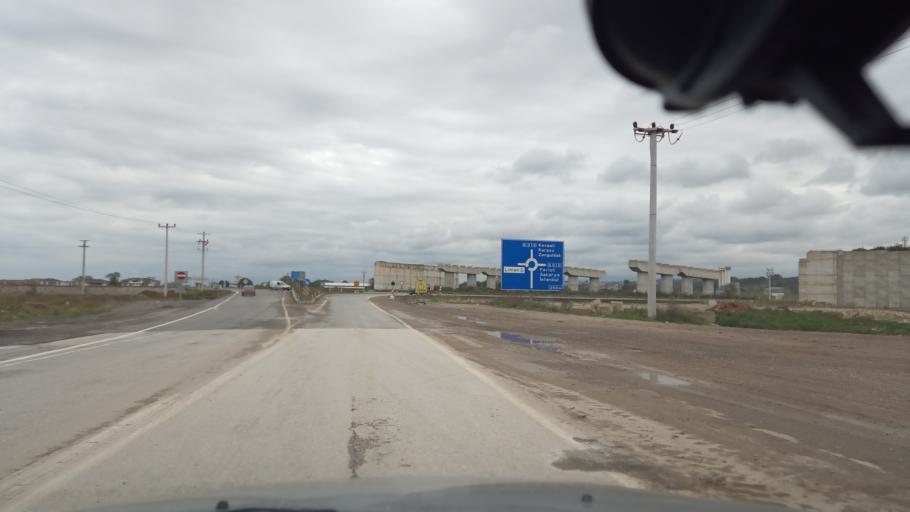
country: TR
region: Sakarya
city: Karasu
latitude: 41.1126
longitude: 30.6587
